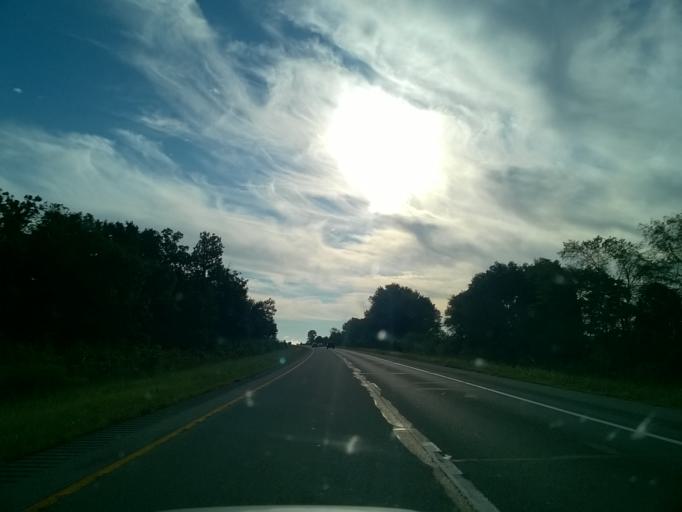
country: US
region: Indiana
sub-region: Spencer County
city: Dale
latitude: 38.1972
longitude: -87.0456
